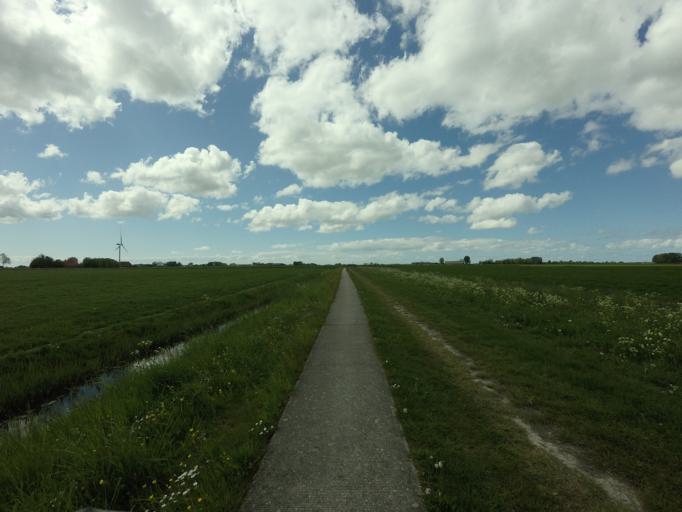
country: NL
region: Friesland
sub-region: Gemeente Franekeradeel
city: Tzum
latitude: 53.1287
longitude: 5.5641
